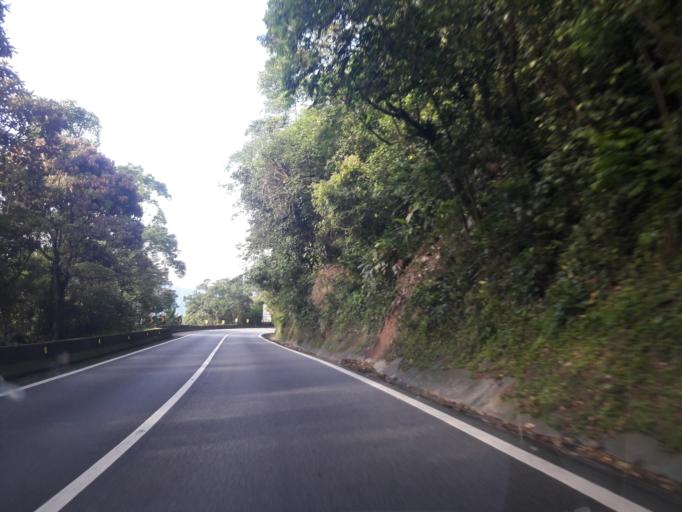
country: BR
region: Sao Paulo
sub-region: Cubatao
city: Cubatao
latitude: -23.8886
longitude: -46.4890
